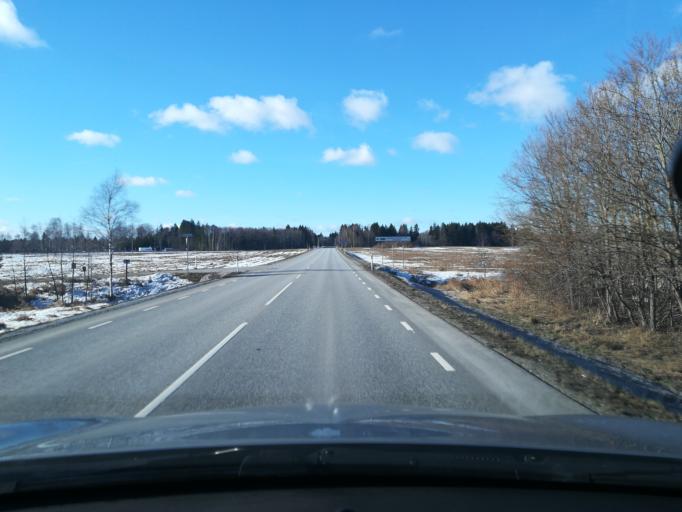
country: EE
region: Harju
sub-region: Saku vald
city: Saku
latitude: 59.2740
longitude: 24.6835
